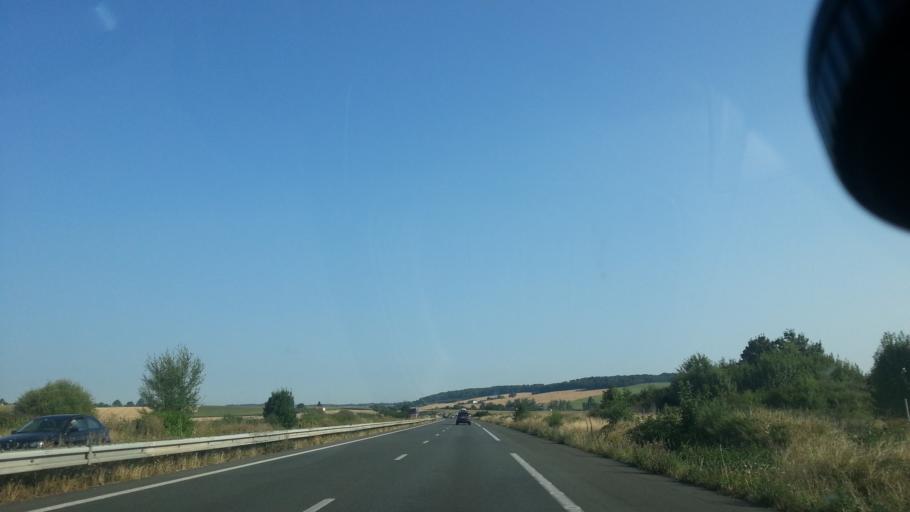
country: FR
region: Poitou-Charentes
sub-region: Departement de la Vienne
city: Antran
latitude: 46.8577
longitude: 0.5258
